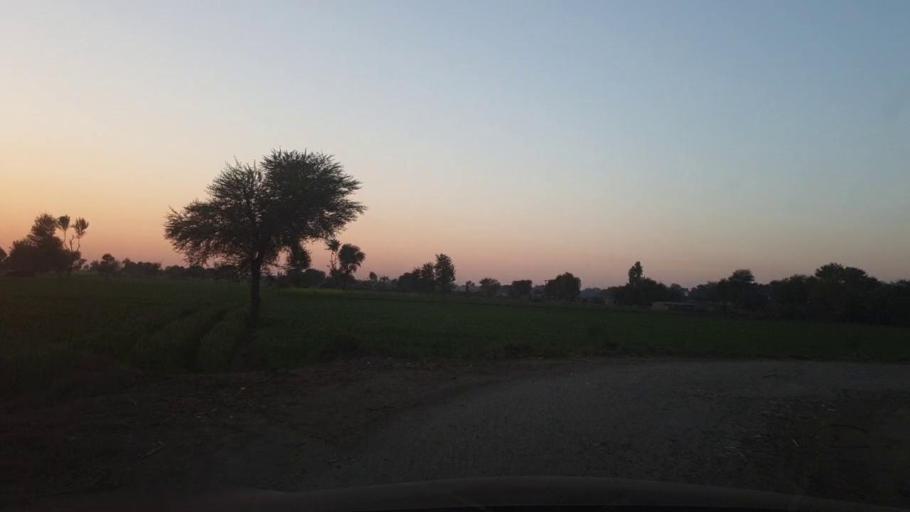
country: PK
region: Sindh
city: Ubauro
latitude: 28.1736
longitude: 69.6354
